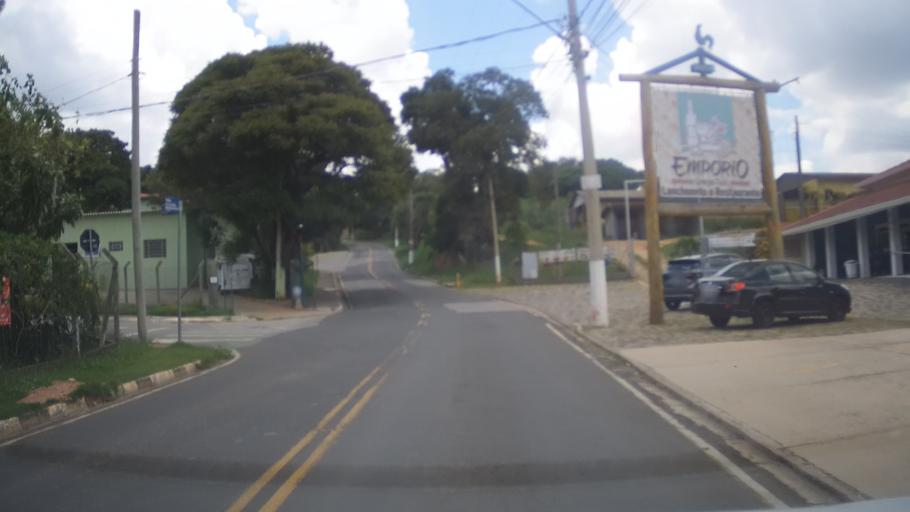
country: BR
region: Sao Paulo
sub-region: Vinhedo
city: Vinhedo
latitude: -23.0478
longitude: -46.9697
